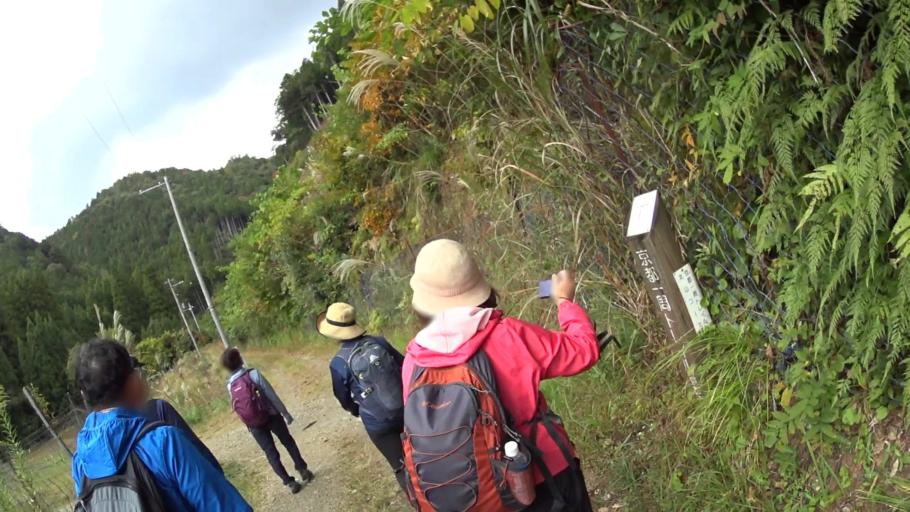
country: JP
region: Kyoto
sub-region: Kyoto-shi
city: Kamigyo-ku
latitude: 35.1104
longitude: 135.7840
